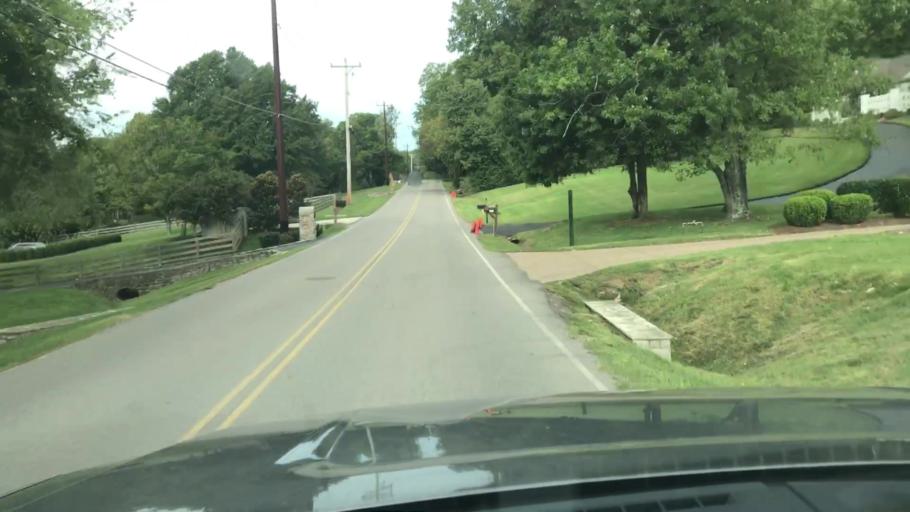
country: US
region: Tennessee
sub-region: Davidson County
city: Forest Hills
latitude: 36.0660
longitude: -86.8159
